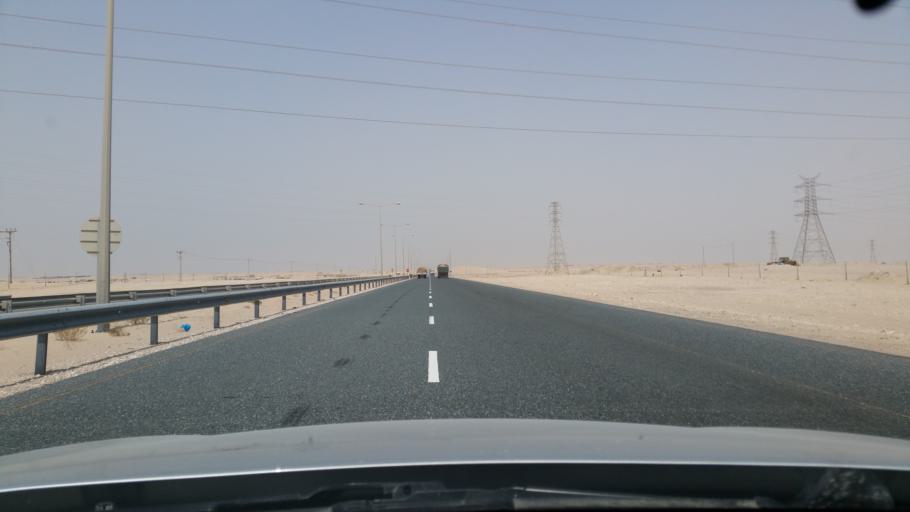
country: QA
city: Umm Bab
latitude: 24.9585
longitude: 50.9684
